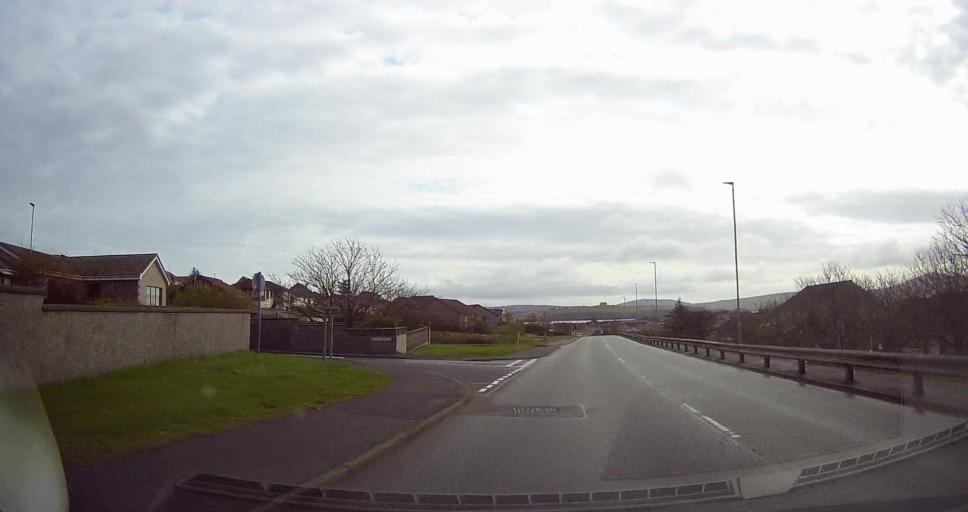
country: GB
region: Scotland
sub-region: Shetland Islands
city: Lerwick
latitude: 60.1440
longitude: -1.1779
